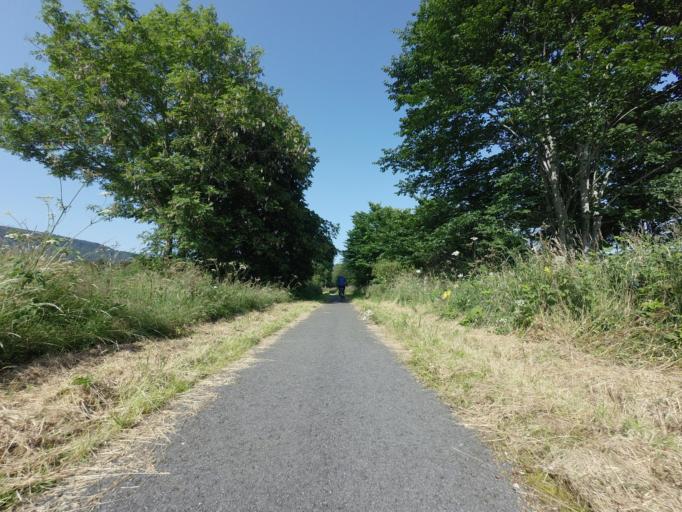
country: GB
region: Scotland
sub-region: Highland
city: Evanton
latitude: 57.6712
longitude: -4.3221
